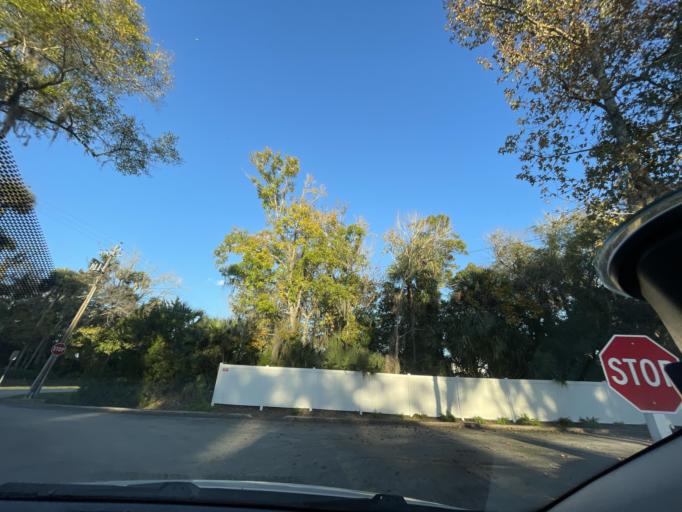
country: US
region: Florida
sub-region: Volusia County
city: Holly Hill
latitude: 29.2239
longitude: -81.0514
